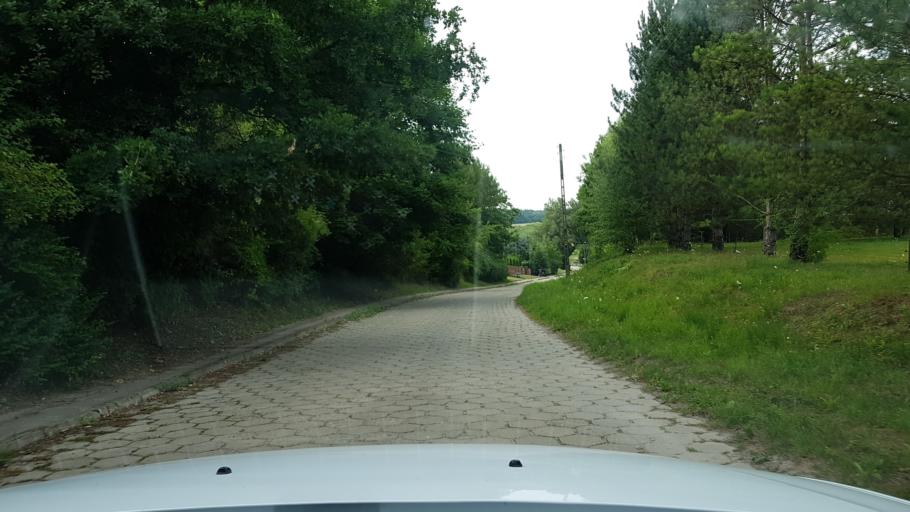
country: PL
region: West Pomeranian Voivodeship
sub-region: Powiat swidwinski
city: Polczyn-Zdroj
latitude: 53.7750
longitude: 16.0939
